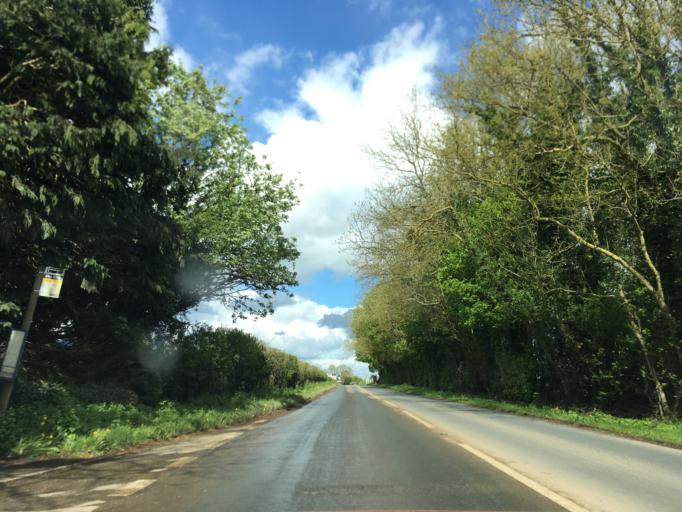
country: GB
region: England
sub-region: Gloucestershire
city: Tetbury
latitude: 51.6126
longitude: -2.1983
